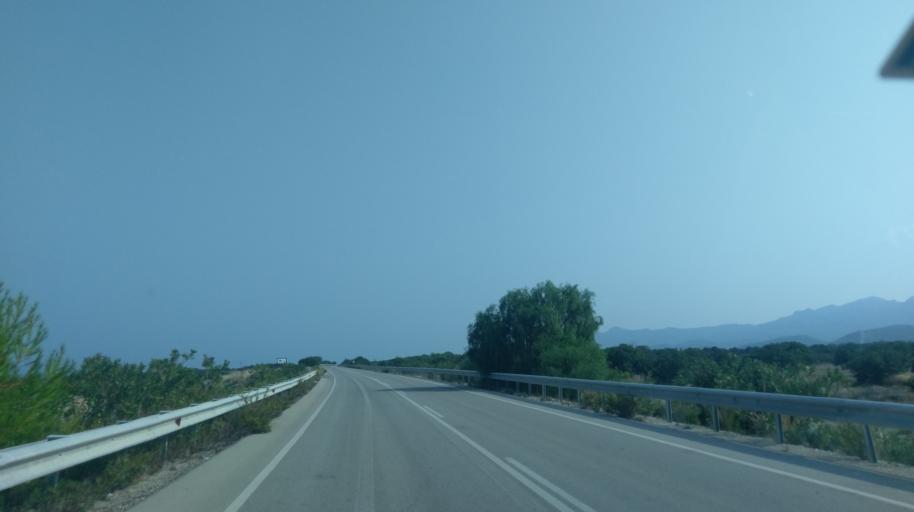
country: CY
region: Ammochostos
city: Trikomo
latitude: 35.4097
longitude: 33.7992
